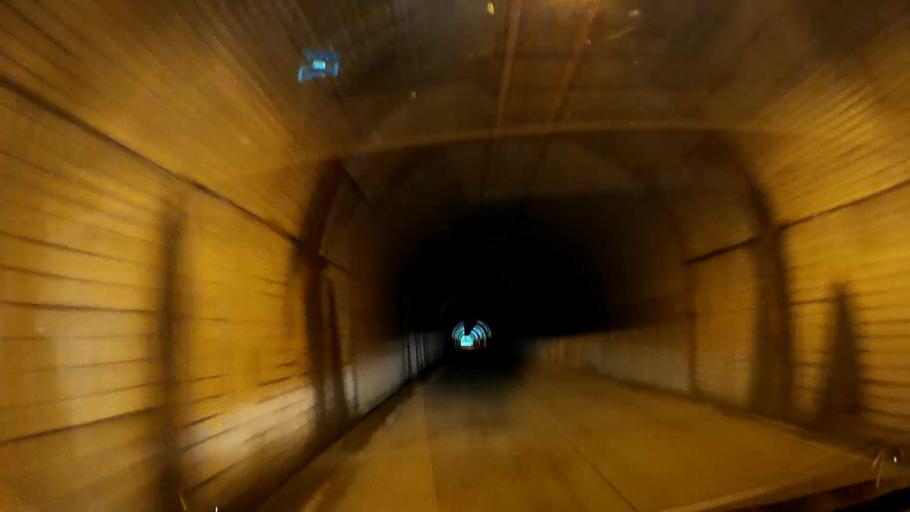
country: JP
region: Shizuoka
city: Shizuoka-shi
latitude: 35.2626
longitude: 138.2302
